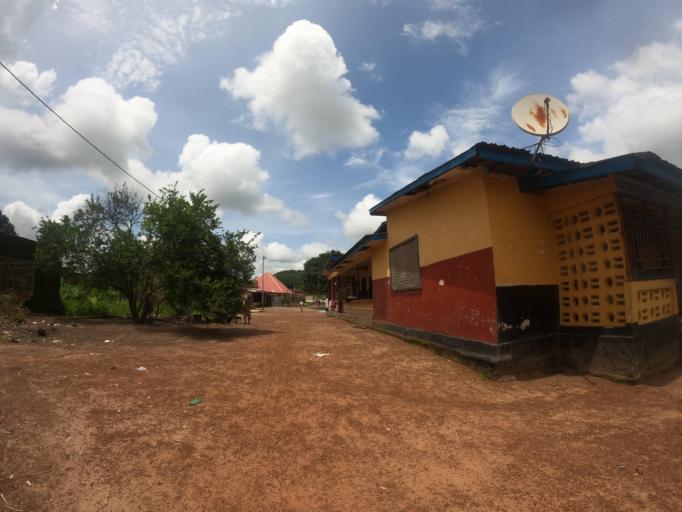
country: SL
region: Northern Province
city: Makeni
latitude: 8.8919
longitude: -12.0531
